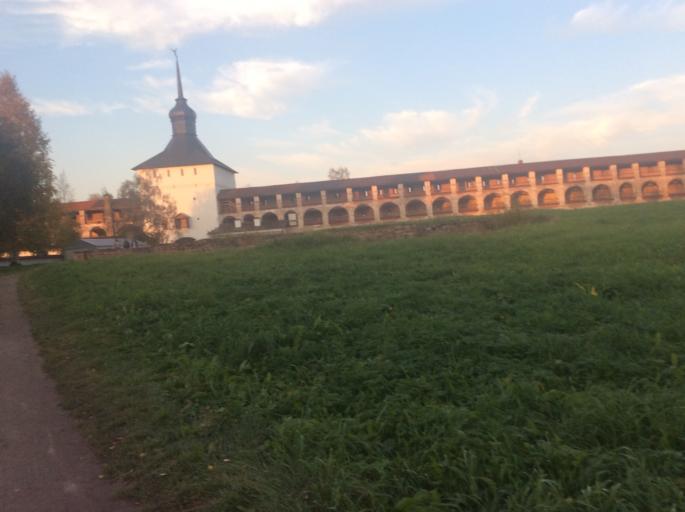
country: RU
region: Vologda
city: Kirillov
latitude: 59.8575
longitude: 38.3693
